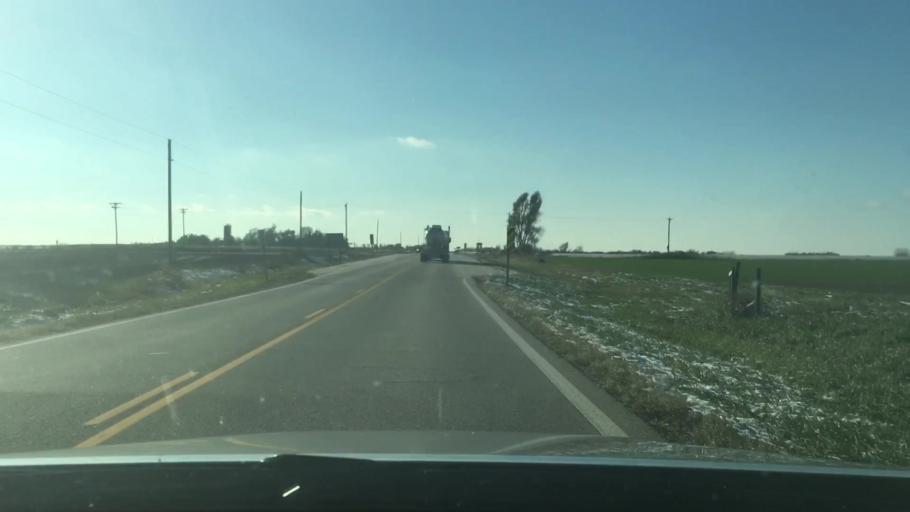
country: US
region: Kansas
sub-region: Rice County
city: Sterling
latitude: 38.1447
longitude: -98.1769
